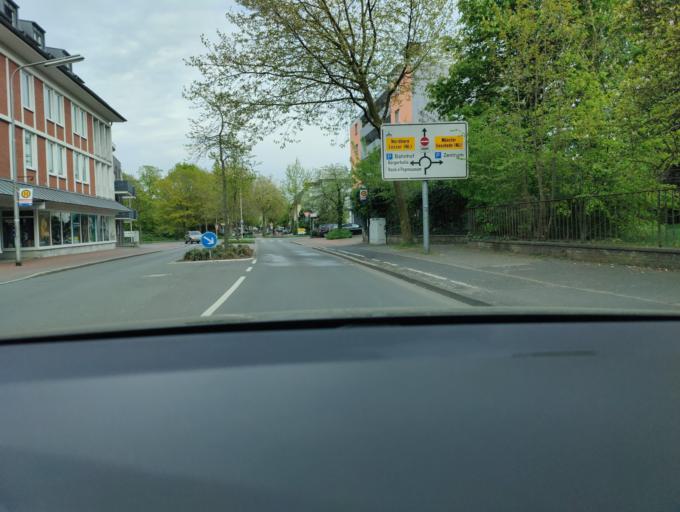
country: DE
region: North Rhine-Westphalia
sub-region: Regierungsbezirk Munster
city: Gronau
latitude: 52.2126
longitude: 7.0179
